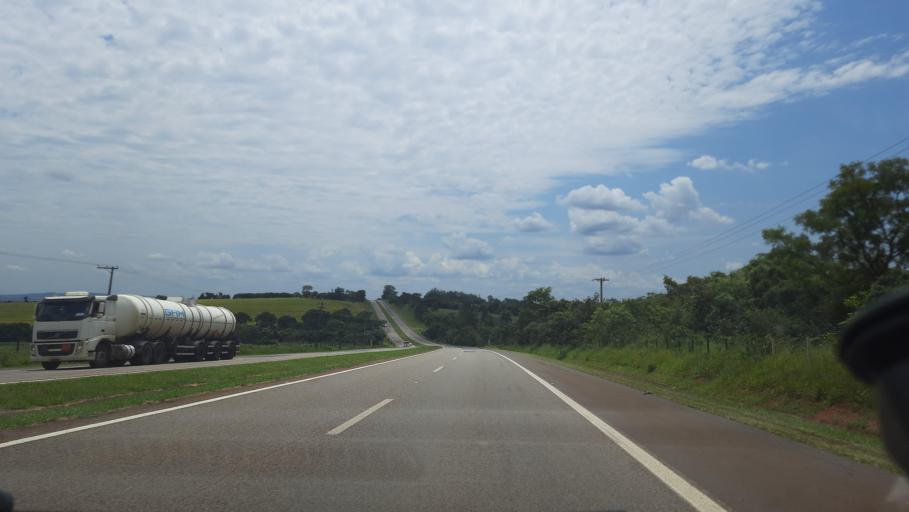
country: BR
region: Sao Paulo
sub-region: Casa Branca
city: Casa Branca
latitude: -21.7350
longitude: -47.0738
